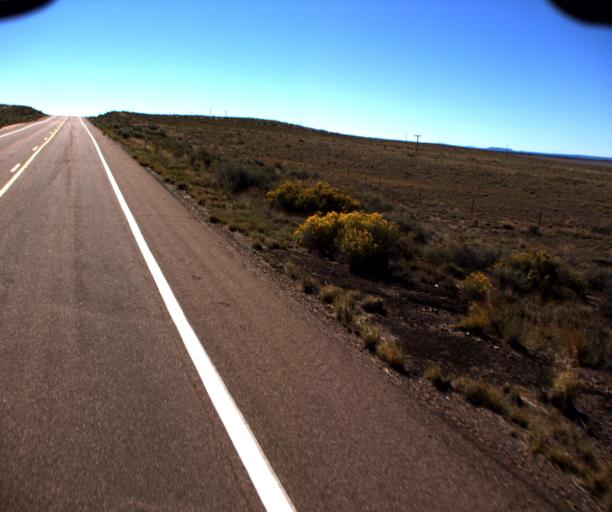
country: US
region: Arizona
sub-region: Navajo County
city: Snowflake
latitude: 34.7551
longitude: -109.8062
